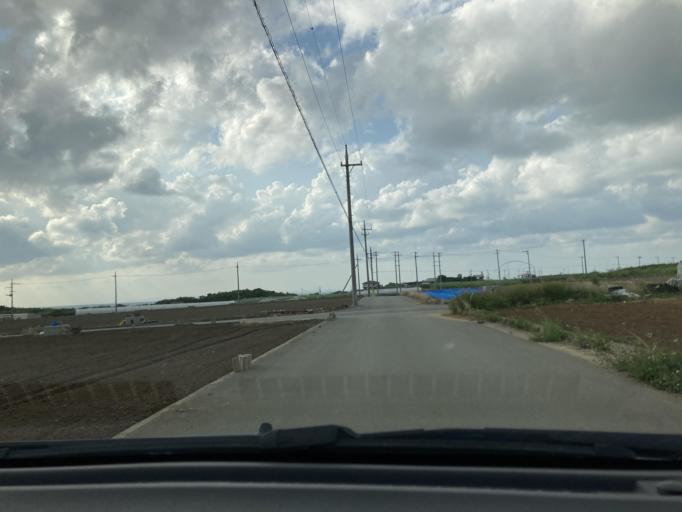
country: JP
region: Okinawa
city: Itoman
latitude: 26.0835
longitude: 127.6673
